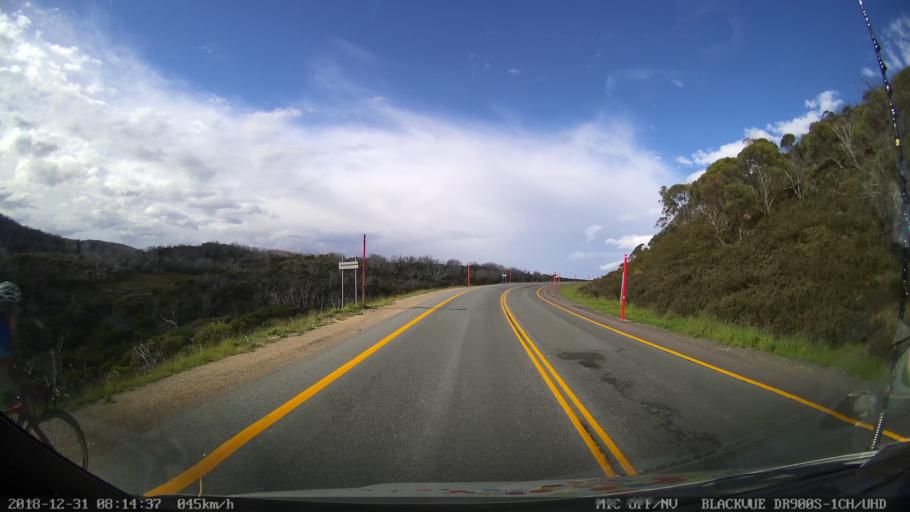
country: AU
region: New South Wales
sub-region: Snowy River
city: Jindabyne
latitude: -36.3963
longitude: 148.4252
